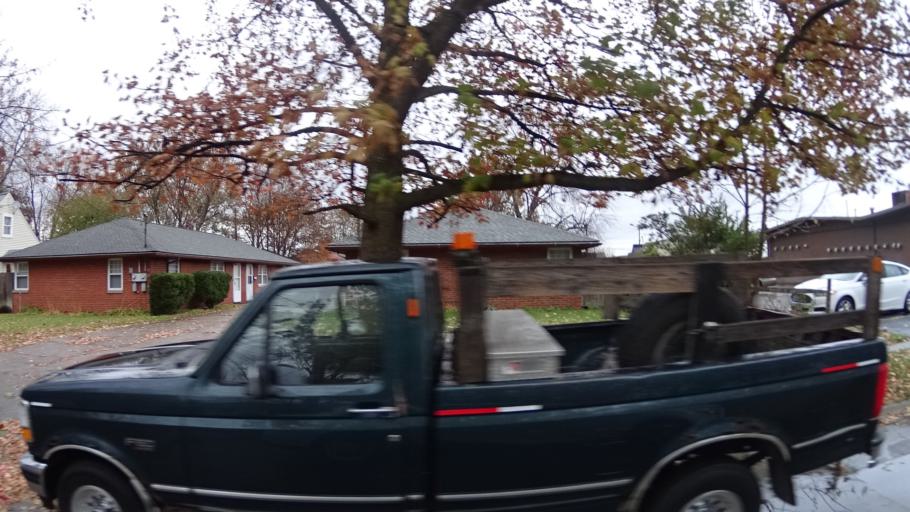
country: US
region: Ohio
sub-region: Lorain County
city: Elyria
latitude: 41.3758
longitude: -82.1294
